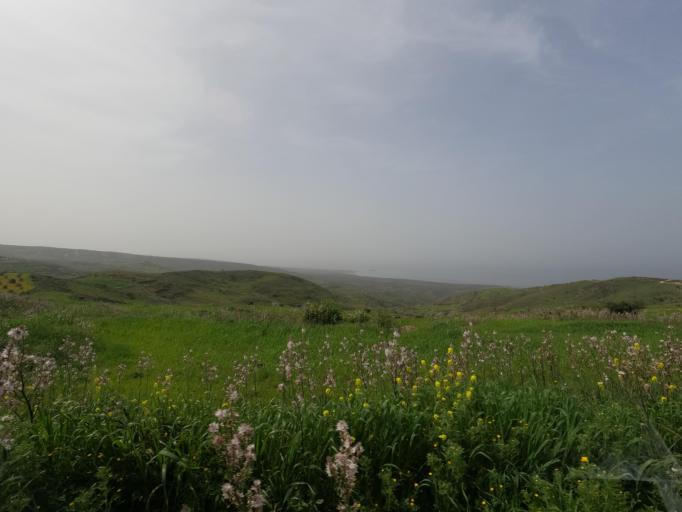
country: CY
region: Pafos
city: Polis
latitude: 34.9765
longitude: 32.3552
